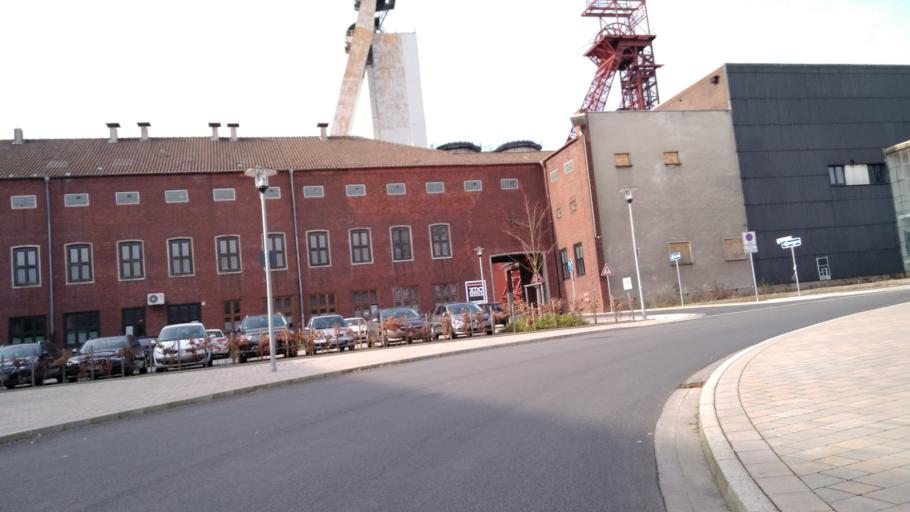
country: DE
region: North Rhine-Westphalia
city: Herten
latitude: 51.6075
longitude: 7.1184
